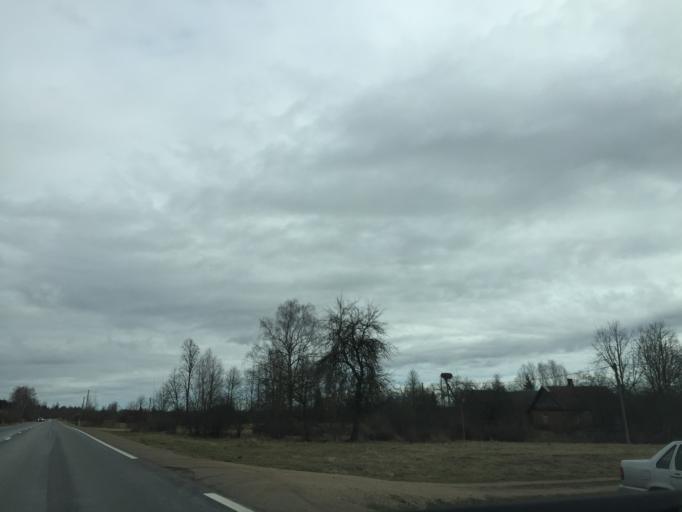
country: LV
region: Daugavpils
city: Daugavpils
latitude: 55.9214
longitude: 26.6764
